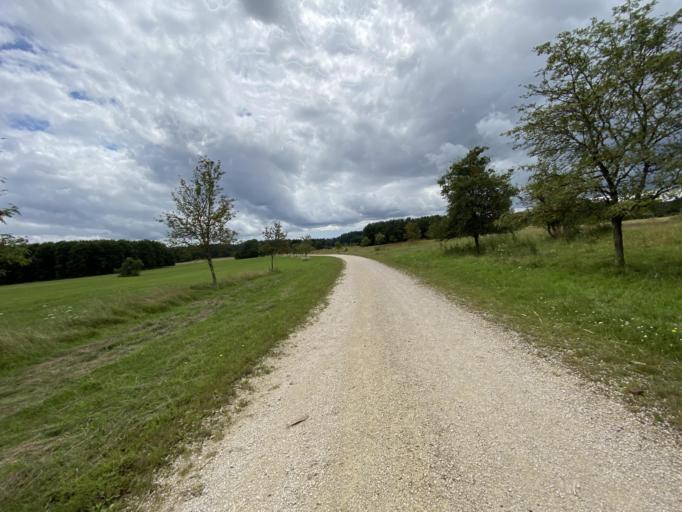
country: DE
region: Baden-Wuerttemberg
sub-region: Tuebingen Region
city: Sigmaringen
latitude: 48.0854
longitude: 9.2442
